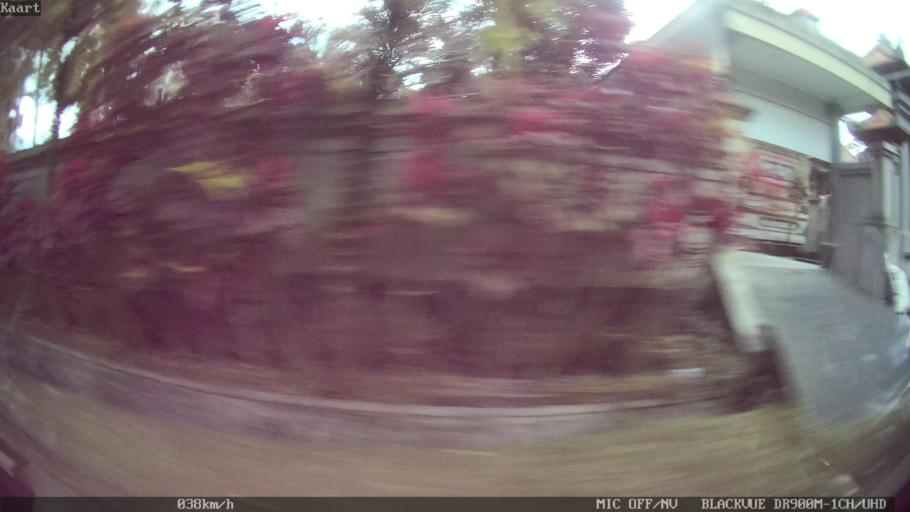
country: ID
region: Bali
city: Banjar Pesalakan
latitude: -8.4897
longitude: 115.3045
